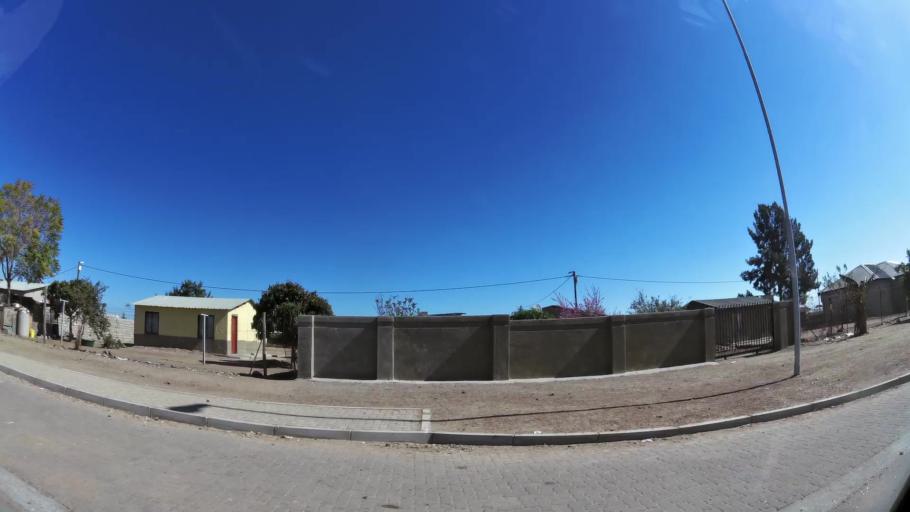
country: ZA
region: Limpopo
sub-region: Capricorn District Municipality
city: Polokwane
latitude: -23.8544
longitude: 29.4132
